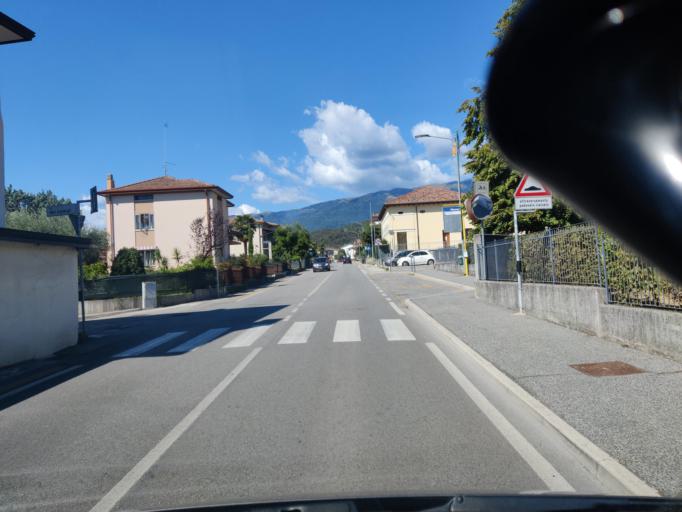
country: IT
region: Veneto
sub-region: Provincia di Treviso
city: Fregona
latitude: 45.9847
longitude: 12.3327
